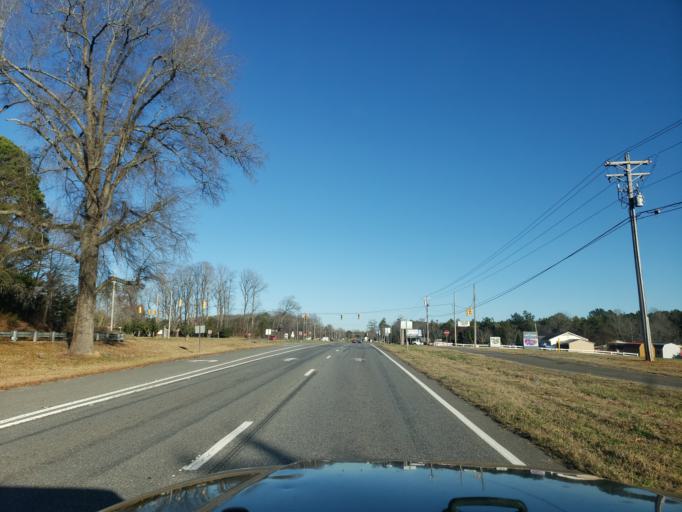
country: US
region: North Carolina
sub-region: Gaston County
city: Bessemer City
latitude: 35.2564
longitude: -81.2603
